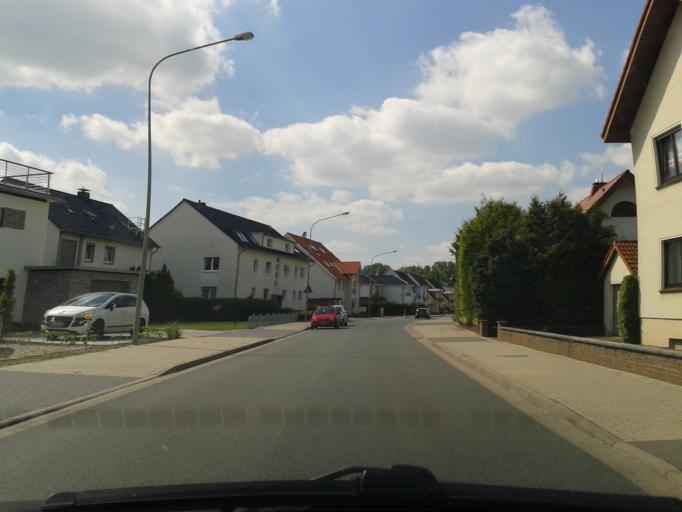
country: DE
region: North Rhine-Westphalia
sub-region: Regierungsbezirk Detmold
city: Paderborn
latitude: 51.7498
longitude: 8.7121
